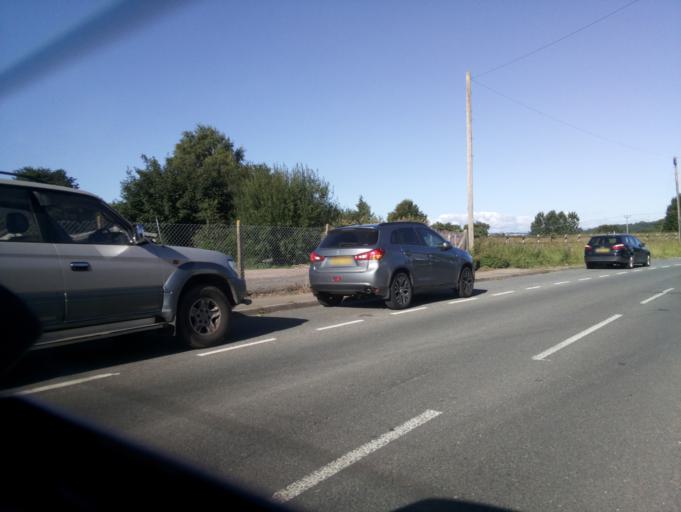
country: GB
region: England
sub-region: Gloucestershire
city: Coleford
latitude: 51.7904
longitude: -2.6010
